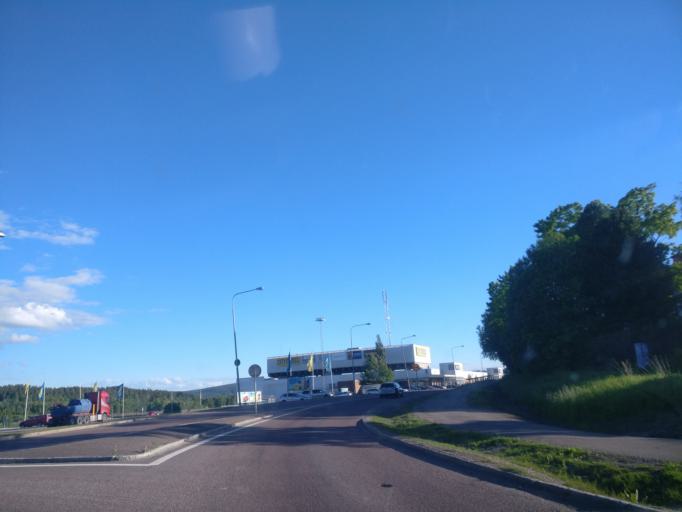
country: SE
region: Vaesternorrland
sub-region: Sundsvalls Kommun
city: Johannedal
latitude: 62.4157
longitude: 17.3413
